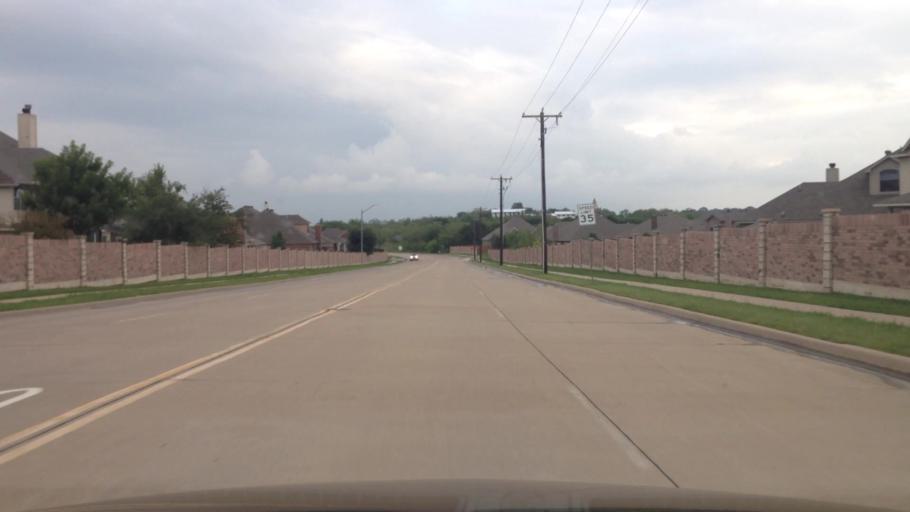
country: US
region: Texas
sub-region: Johnson County
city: Burleson
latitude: 32.5711
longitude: -97.3323
